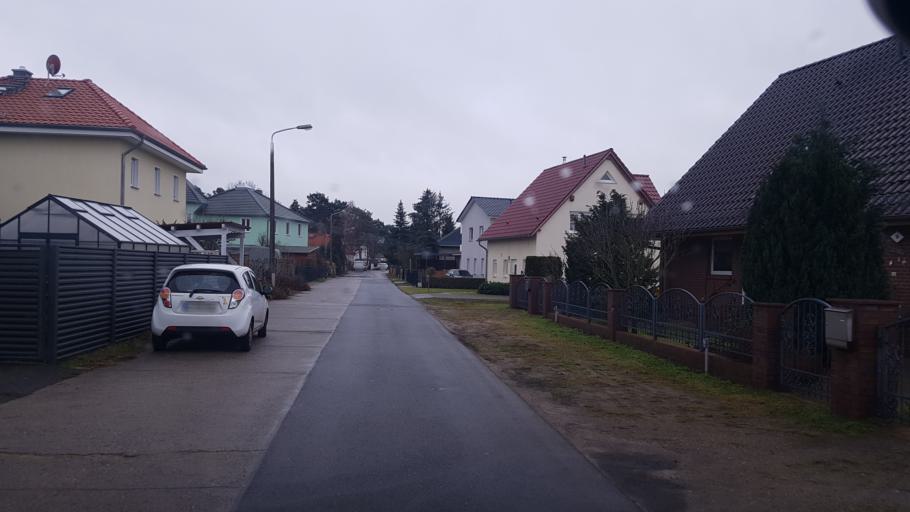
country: DE
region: Berlin
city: Wannsee
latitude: 52.3592
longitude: 13.1287
